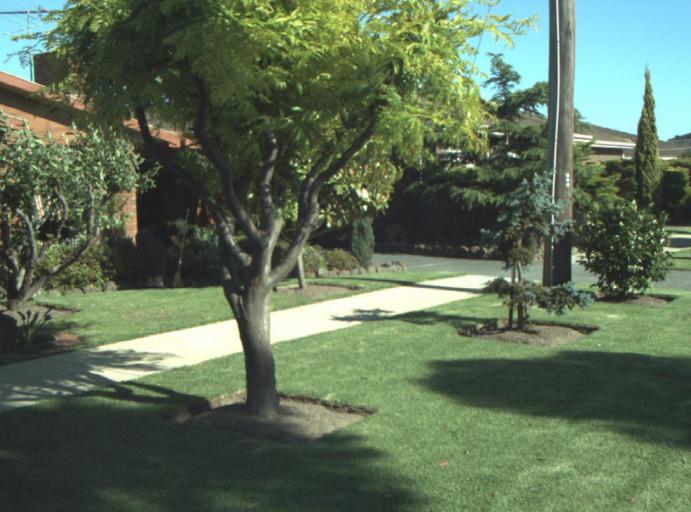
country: AU
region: Victoria
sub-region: Greater Geelong
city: Hamlyn Heights
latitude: -38.1129
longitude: 144.3228
